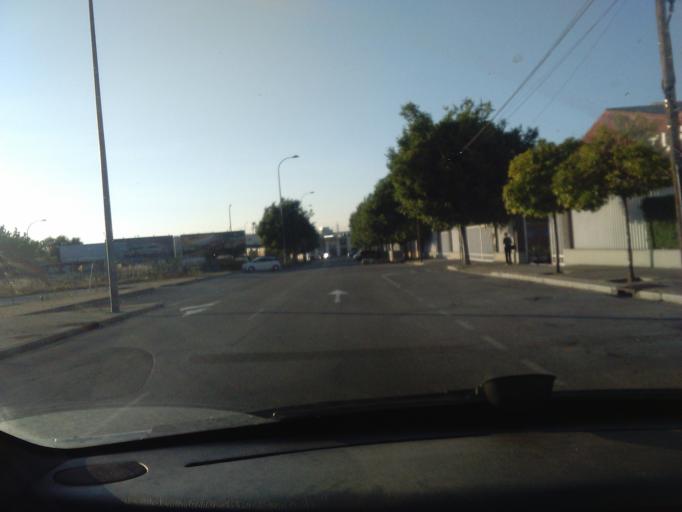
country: ES
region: Andalusia
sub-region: Provincia de Sevilla
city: Sevilla
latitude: 37.3933
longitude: -5.9464
